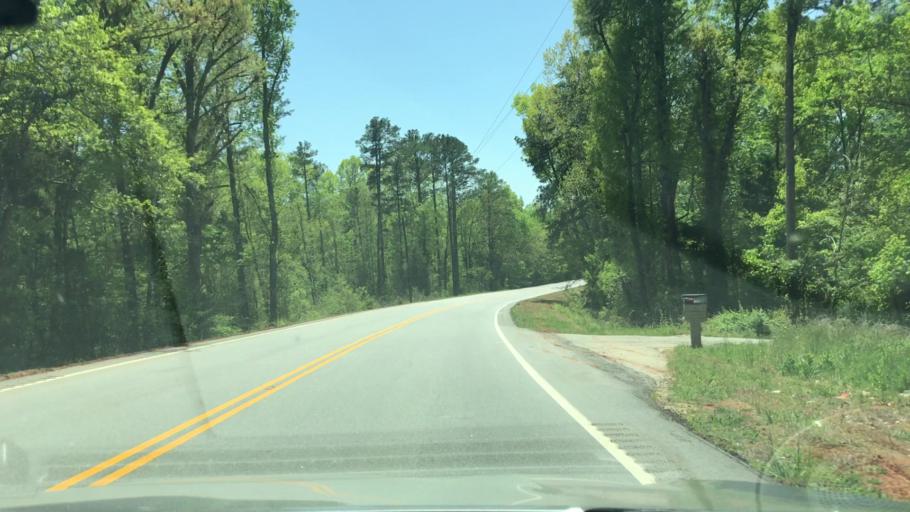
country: US
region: South Carolina
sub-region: Union County
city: Buffalo
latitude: 34.6724
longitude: -81.7334
